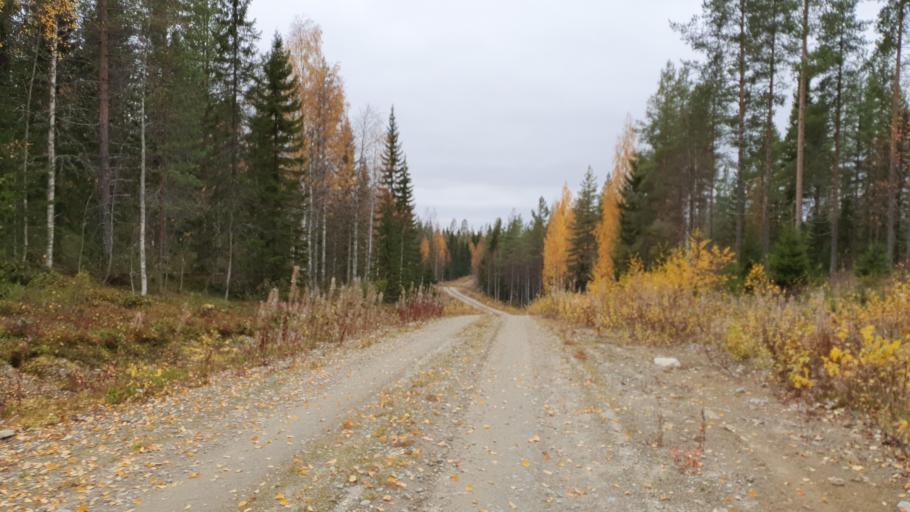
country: FI
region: Kainuu
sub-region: Kehys-Kainuu
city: Kuhmo
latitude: 64.4451
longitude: 29.6274
